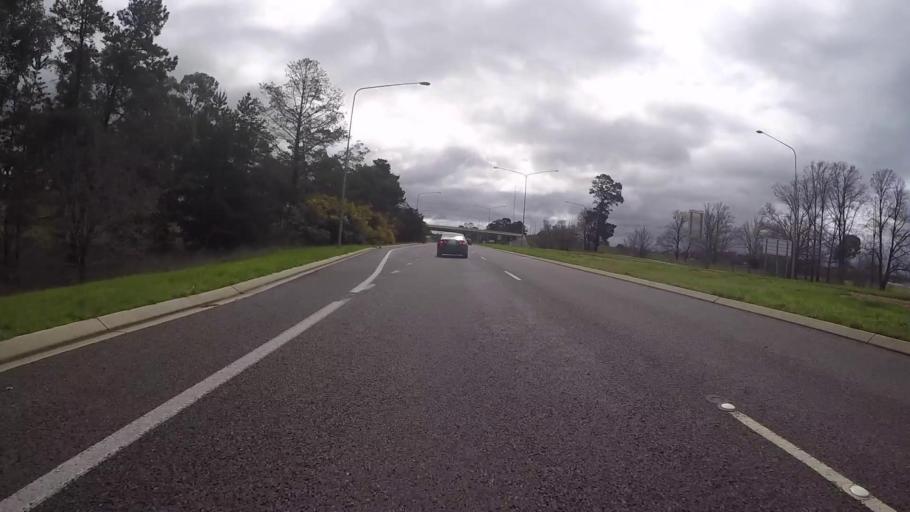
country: AU
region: Australian Capital Territory
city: Kaleen
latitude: -35.2279
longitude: 149.1232
